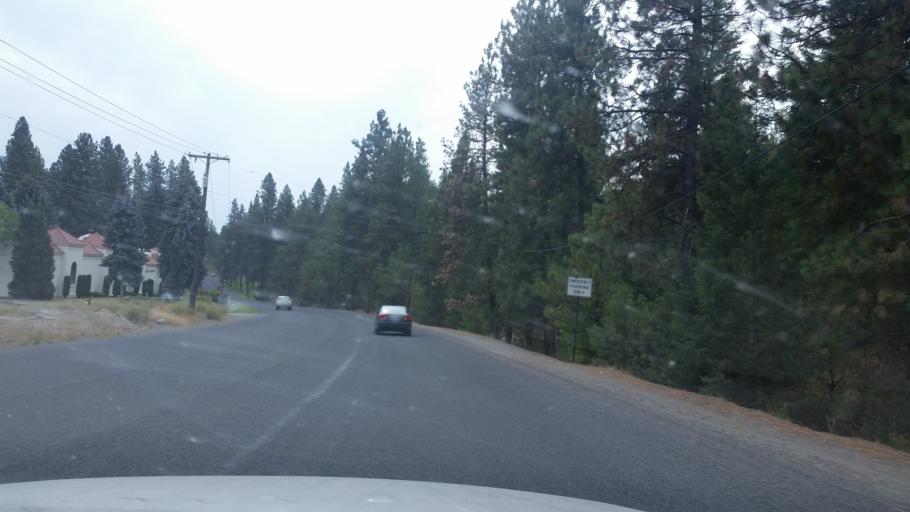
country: US
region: Washington
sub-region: Spokane County
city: Spokane
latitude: 47.6635
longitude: -117.4688
